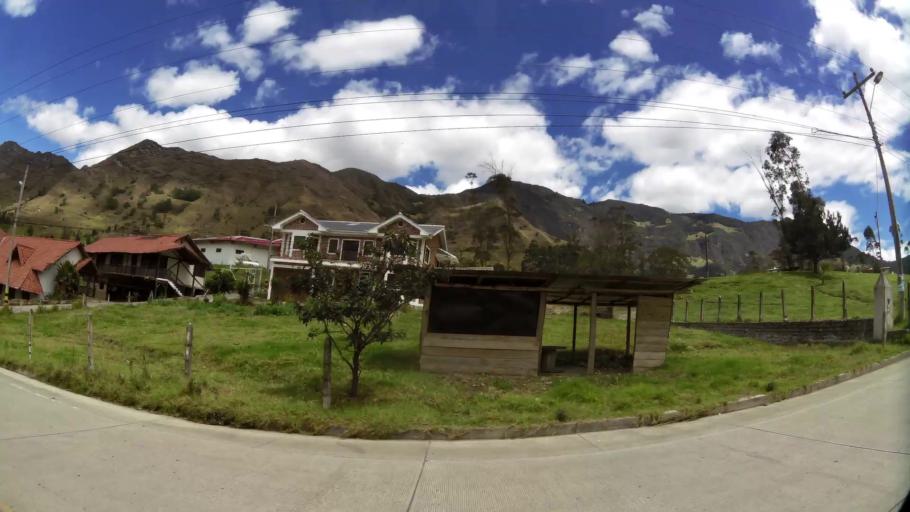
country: EC
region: Azuay
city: Cuenca
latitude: -3.1375
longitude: -79.1346
